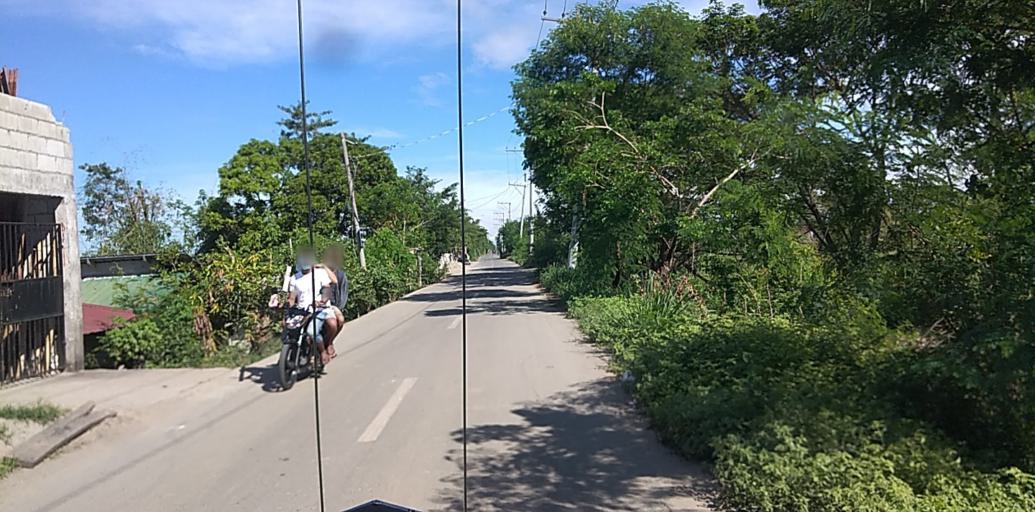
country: PH
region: Central Luzon
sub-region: Province of Pampanga
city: Candaba
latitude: 15.0796
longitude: 120.8086
